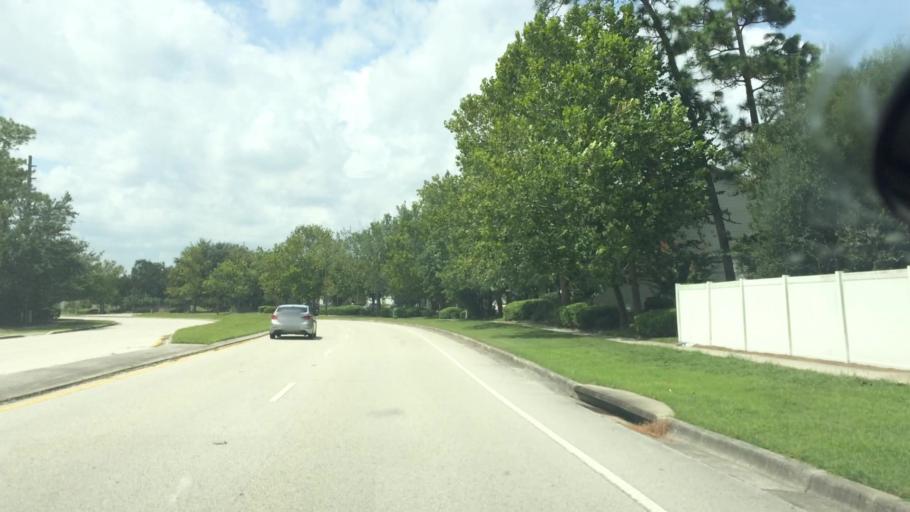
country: US
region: Florida
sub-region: Osceola County
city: Saint Cloud
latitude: 28.2286
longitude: -81.3136
